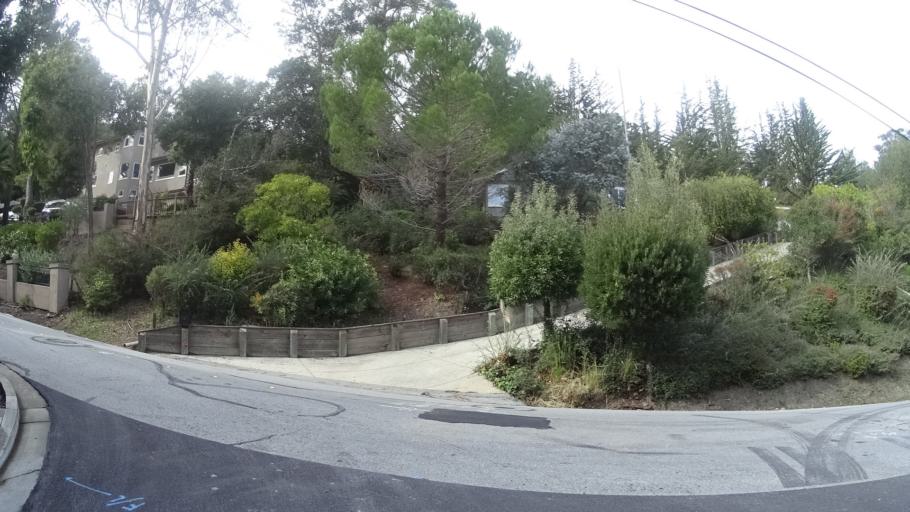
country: US
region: California
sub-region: San Mateo County
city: Hillsborough
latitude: 37.5732
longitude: -122.3885
